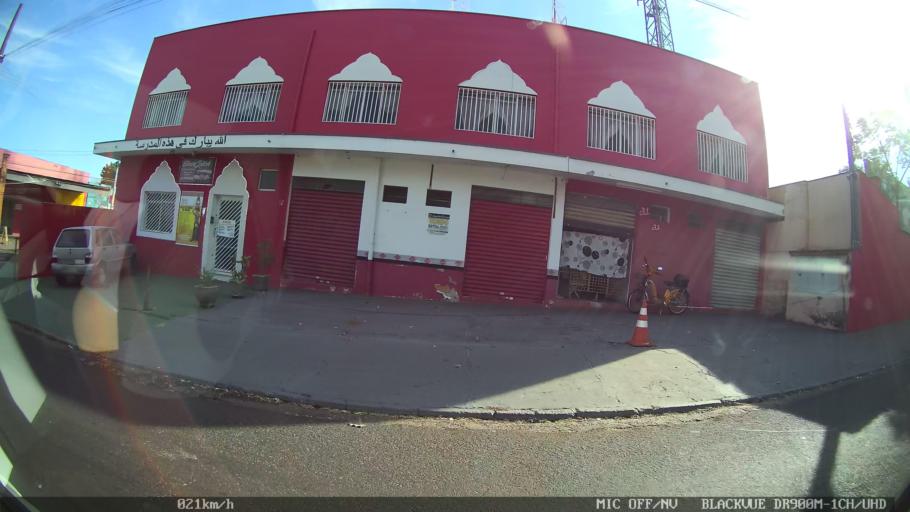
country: BR
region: Sao Paulo
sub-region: Araraquara
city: Araraquara
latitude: -21.7910
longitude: -48.1571
